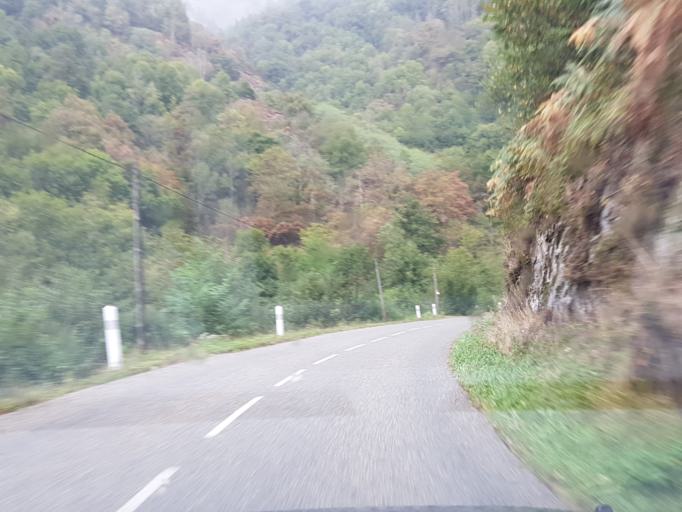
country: FR
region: Midi-Pyrenees
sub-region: Departement de l'Ariege
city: Saint-Girons
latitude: 42.9099
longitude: 1.2811
